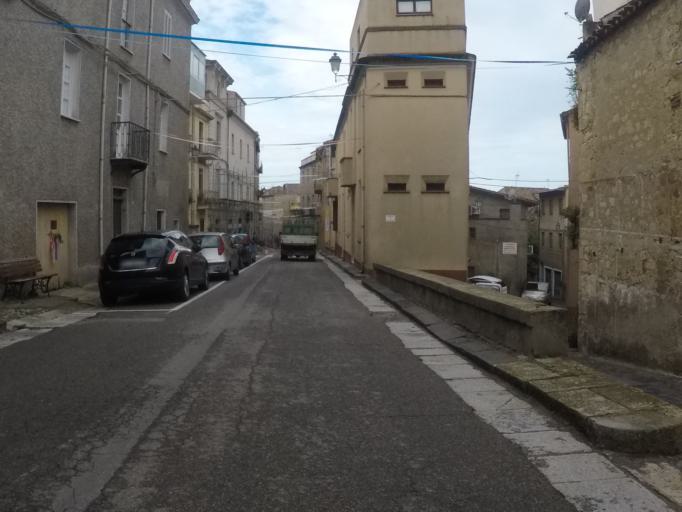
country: IT
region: Sardinia
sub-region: Provincia di Oristano
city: Cuglieri
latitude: 40.1909
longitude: 8.5686
